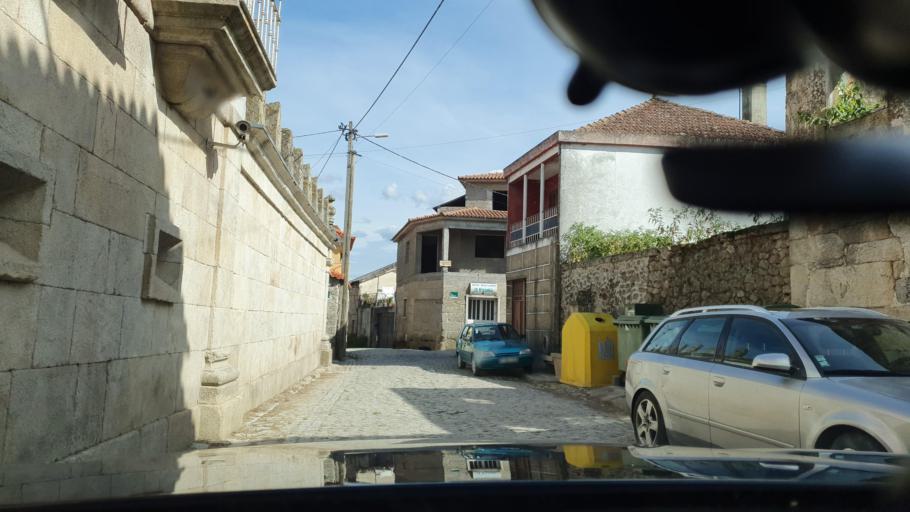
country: PT
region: Vila Real
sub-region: Boticas
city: Boticas
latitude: 41.7090
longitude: -7.5667
